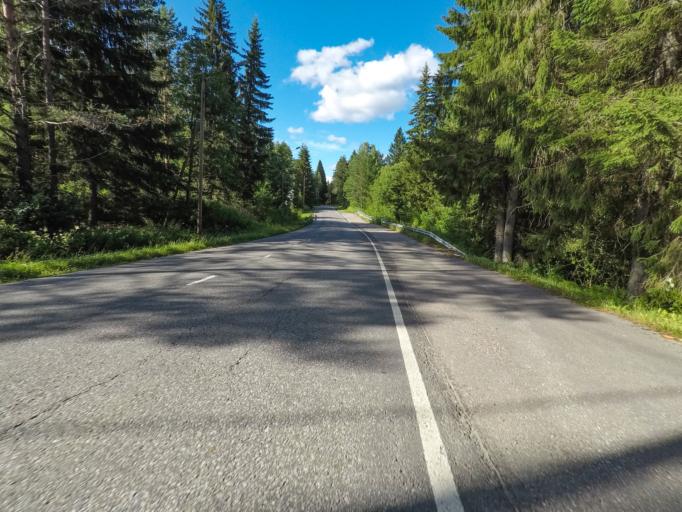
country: FI
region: South Karelia
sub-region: Imatra
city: Imatra
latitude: 61.1484
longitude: 28.7529
